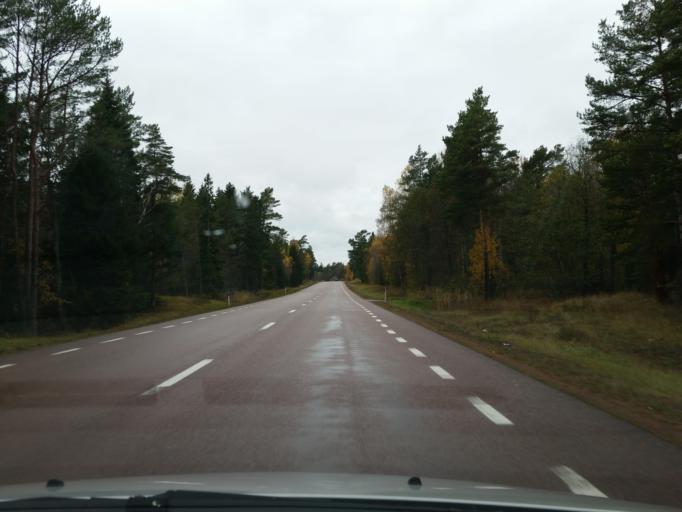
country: AX
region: Alands landsbygd
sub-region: Lumparland
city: Lumparland
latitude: 60.0851
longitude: 20.2483
